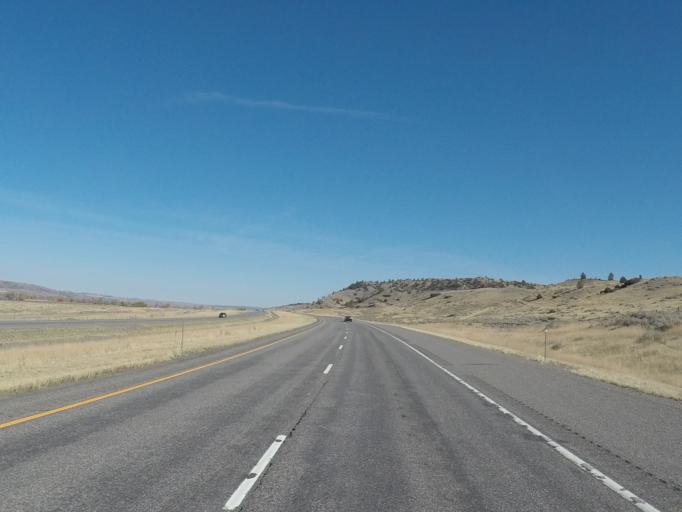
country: US
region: Montana
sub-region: Sweet Grass County
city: Big Timber
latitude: 45.7658
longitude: -110.0905
